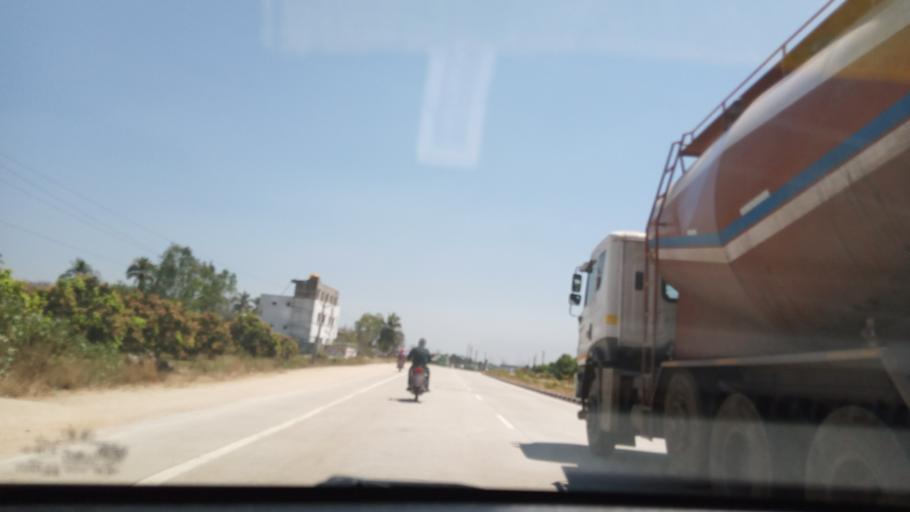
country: IN
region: Andhra Pradesh
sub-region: Chittoor
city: Chittoor
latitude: 13.1959
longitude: 79.0066
